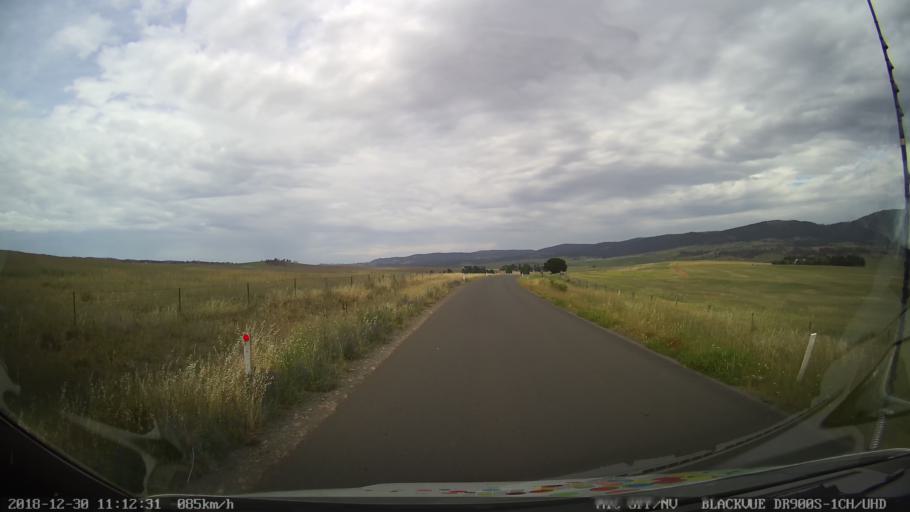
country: AU
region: New South Wales
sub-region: Snowy River
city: Jindabyne
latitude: -36.5290
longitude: 148.7558
